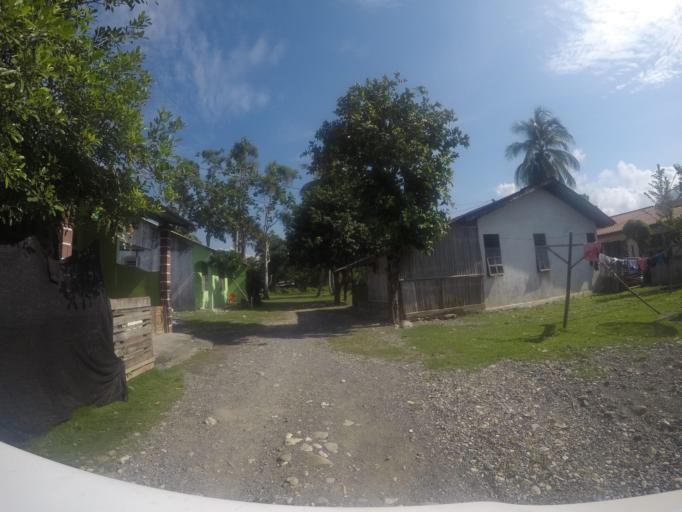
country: TL
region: Viqueque
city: Viqueque
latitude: -8.8559
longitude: 126.3617
